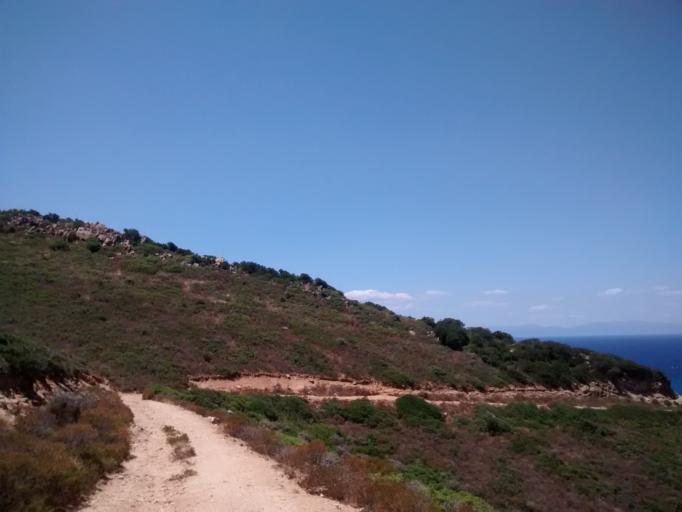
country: IT
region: Sardinia
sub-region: Provincia di Cagliari
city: Villasimius
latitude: 39.1308
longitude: 9.4375
